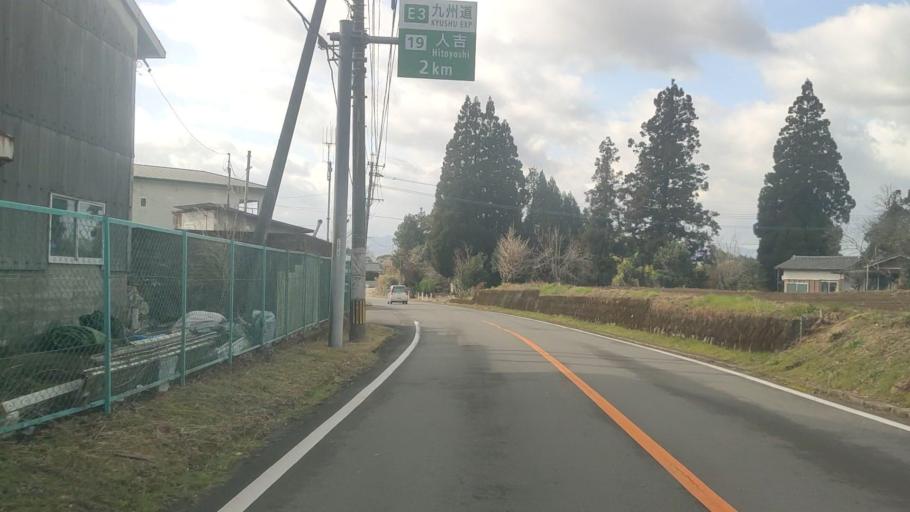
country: JP
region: Kumamoto
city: Hitoyoshi
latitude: 32.2302
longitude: 130.7844
